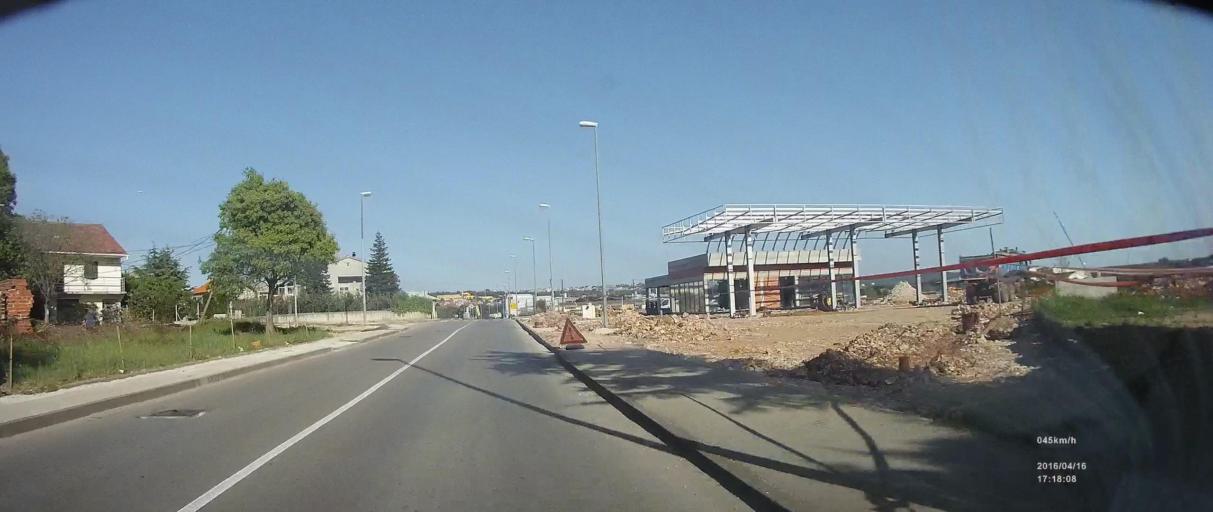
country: HR
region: Zadarska
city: Zadar
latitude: 44.1018
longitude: 15.2530
